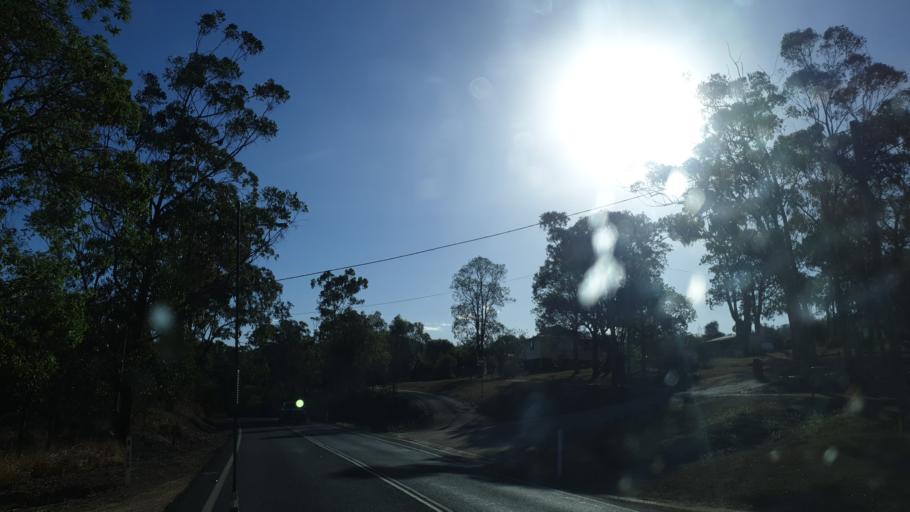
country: AU
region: Queensland
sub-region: Tablelands
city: Atherton
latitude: -17.3700
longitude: 145.3866
